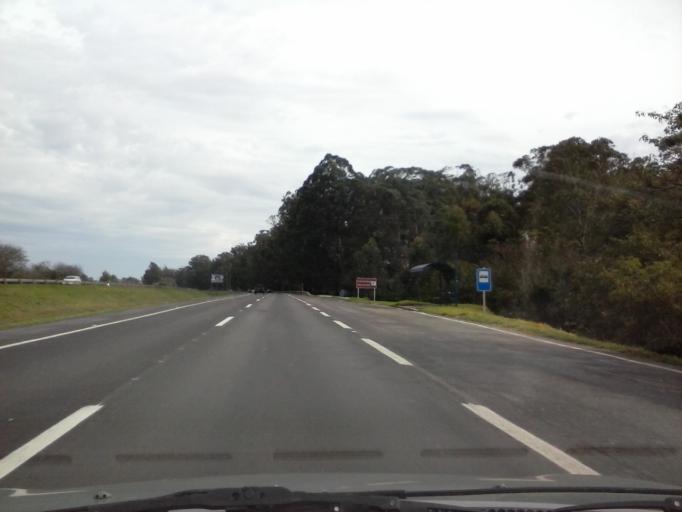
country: BR
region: Rio Grande do Sul
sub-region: Porto Alegre
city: Porto Alegre
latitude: -29.9866
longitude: -51.2418
